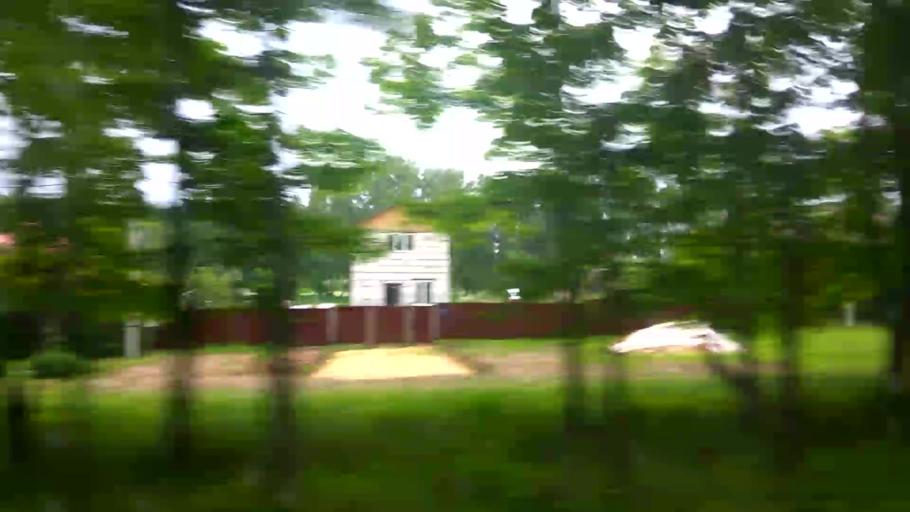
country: RU
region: Moskovskaya
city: Ozherel'ye
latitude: 54.8345
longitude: 38.2790
